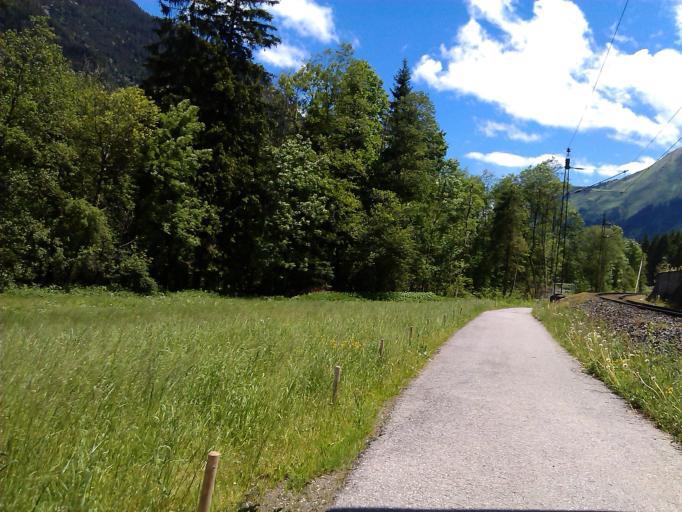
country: AT
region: Tyrol
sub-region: Politischer Bezirk Reutte
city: Bichlbach
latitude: 47.4295
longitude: 10.7715
